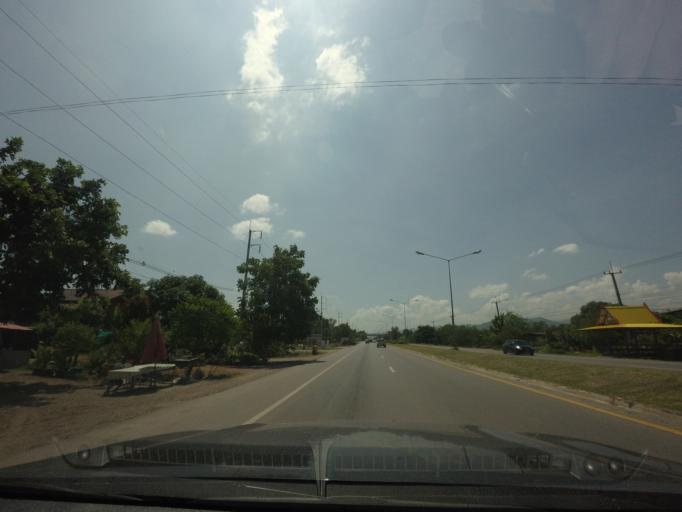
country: TH
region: Phetchabun
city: Lom Sak
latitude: 16.7037
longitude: 101.1743
